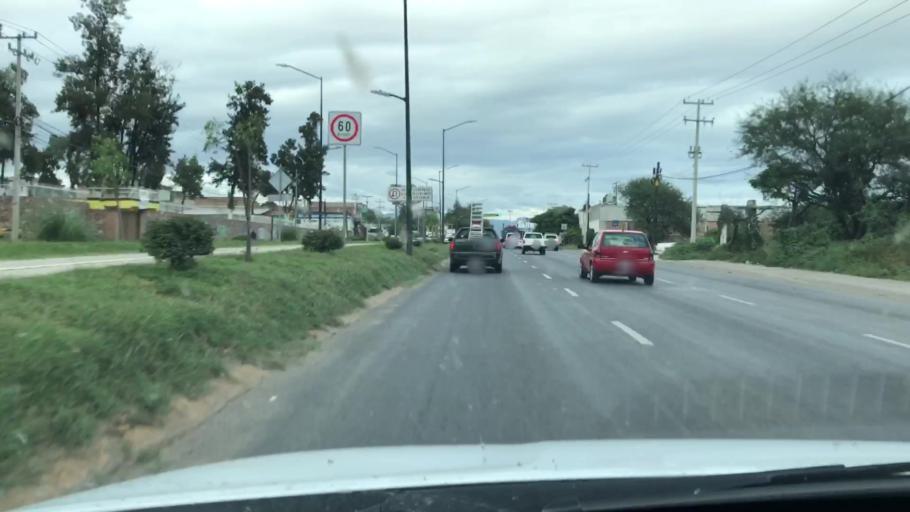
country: MX
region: Guanajuato
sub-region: Leon
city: Centro Familiar la Soledad
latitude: 21.0951
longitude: -101.7295
